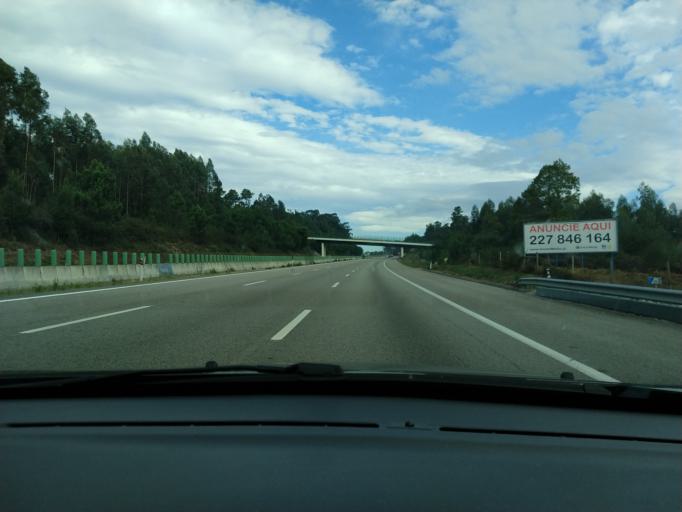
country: PT
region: Aveiro
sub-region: Santa Maria da Feira
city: Feira
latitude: 40.8960
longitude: -8.5682
